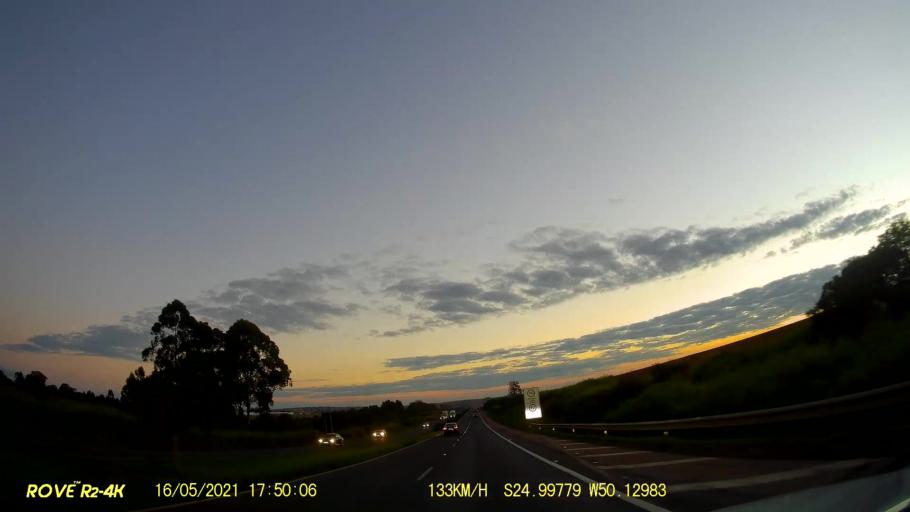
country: BR
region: Parana
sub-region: Carambei
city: Carambei
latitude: -24.9978
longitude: -50.1297
